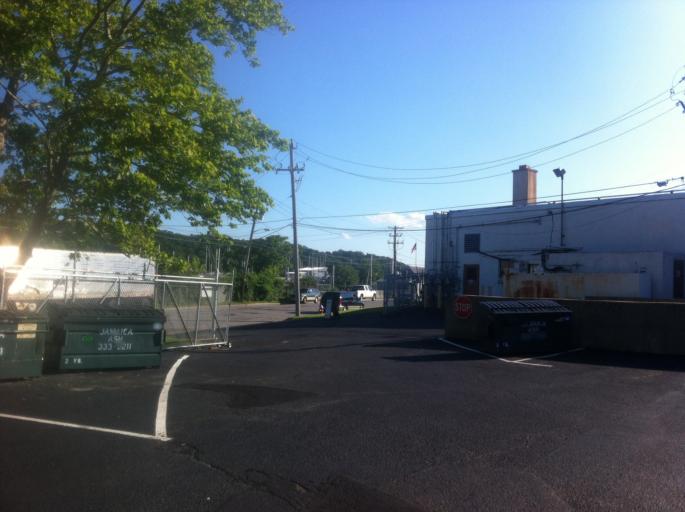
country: US
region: New York
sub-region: Nassau County
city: Glen Cove
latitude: 40.8597
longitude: -73.6419
